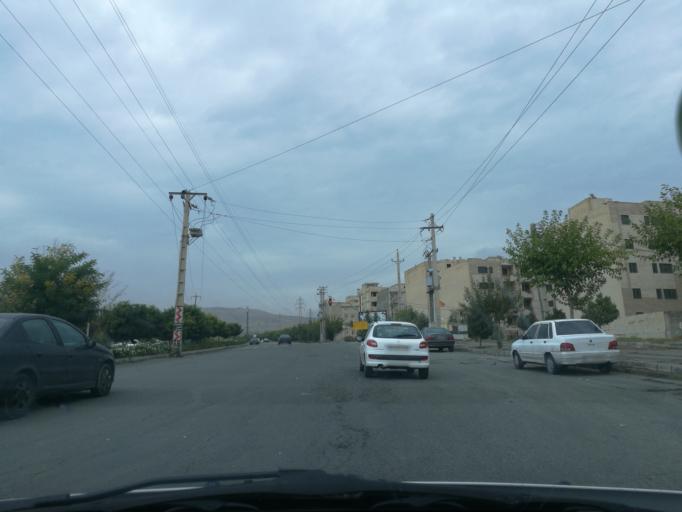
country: IR
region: Alborz
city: Karaj
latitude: 35.8624
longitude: 50.9259
